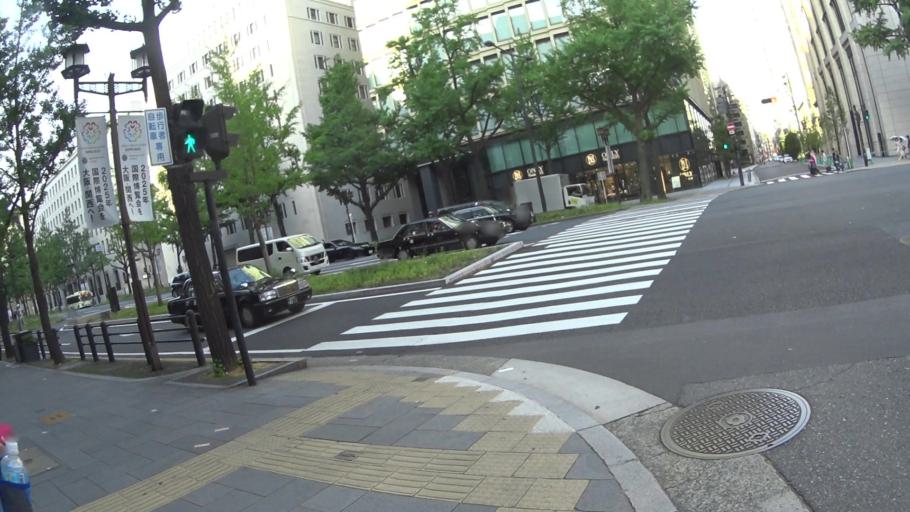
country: JP
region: Osaka
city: Osaka-shi
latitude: 34.6905
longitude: 135.5003
